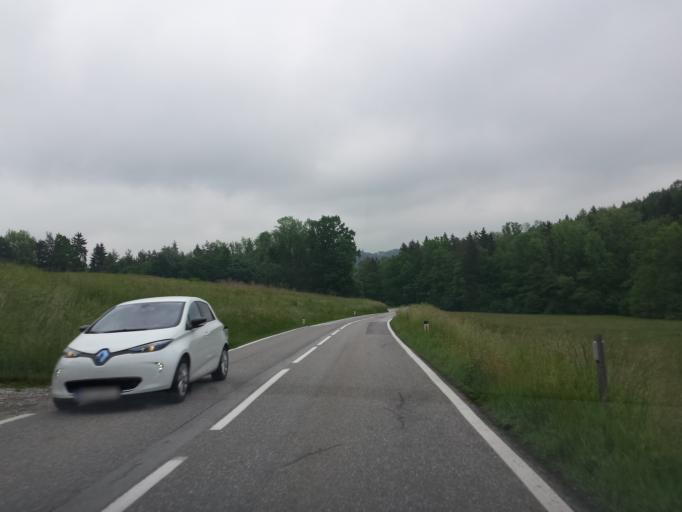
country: AT
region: Styria
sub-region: Politischer Bezirk Graz-Umgebung
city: Kumberg
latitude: 47.1427
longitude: 15.5372
